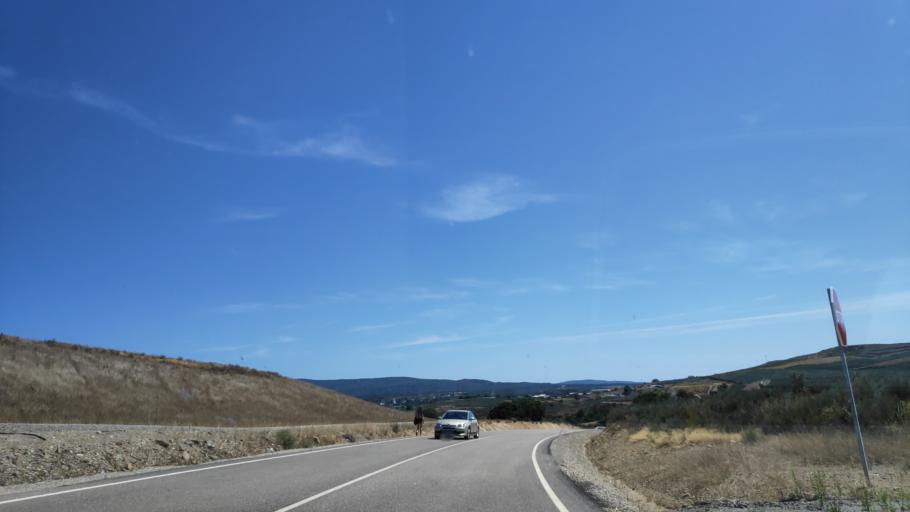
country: ES
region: Castille and Leon
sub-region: Provincia de Zamora
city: Puebla de Sanabria
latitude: 42.0463
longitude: -6.6511
